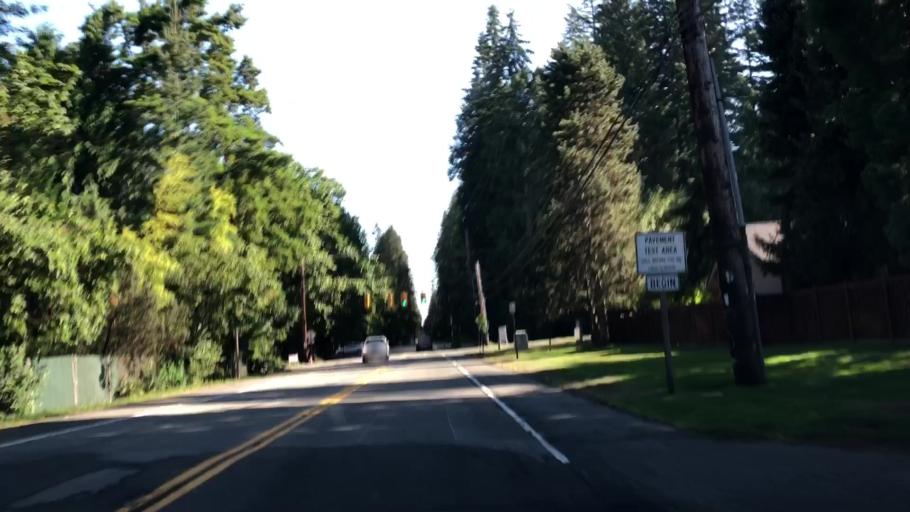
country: US
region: Washington
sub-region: King County
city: Cottage Lake
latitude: 47.7419
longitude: -122.0772
